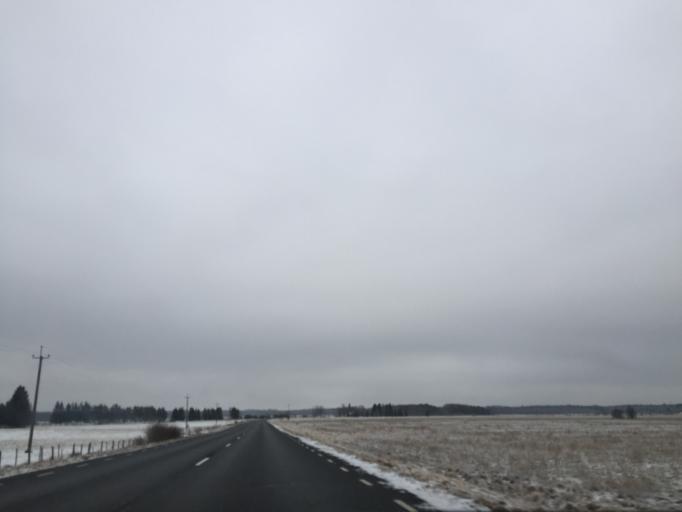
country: EE
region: Laeaene
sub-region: Lihula vald
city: Lihula
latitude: 58.6716
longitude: 23.8259
